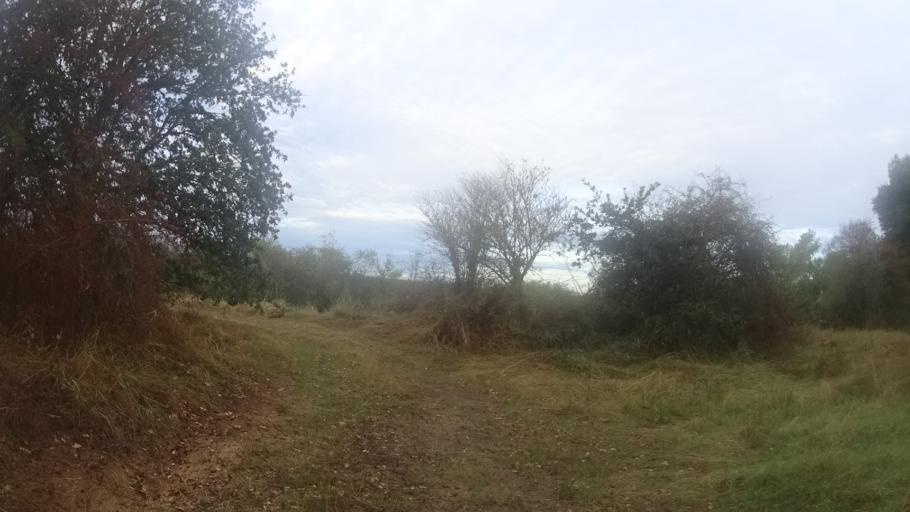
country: FR
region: Centre
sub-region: Departement du Loiret
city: Ouzouer-sur-Loire
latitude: 47.7513
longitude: 2.4744
